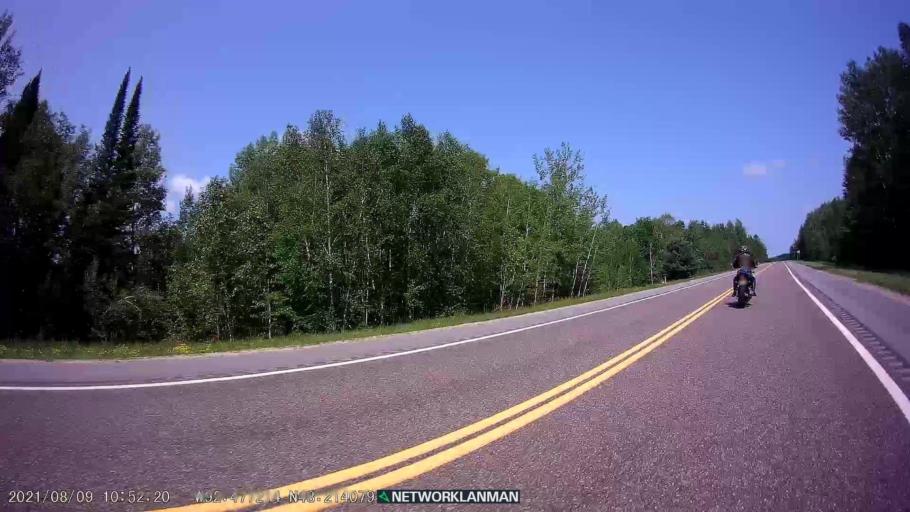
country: US
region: Minnesota
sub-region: Saint Louis County
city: Ely
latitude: 48.2143
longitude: -92.4771
